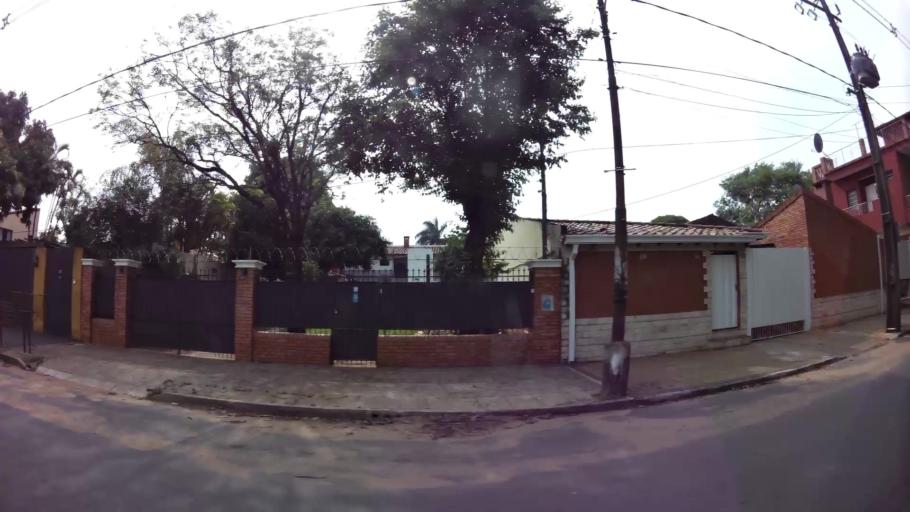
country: PY
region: Central
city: Fernando de la Mora
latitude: -25.3003
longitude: -57.5567
